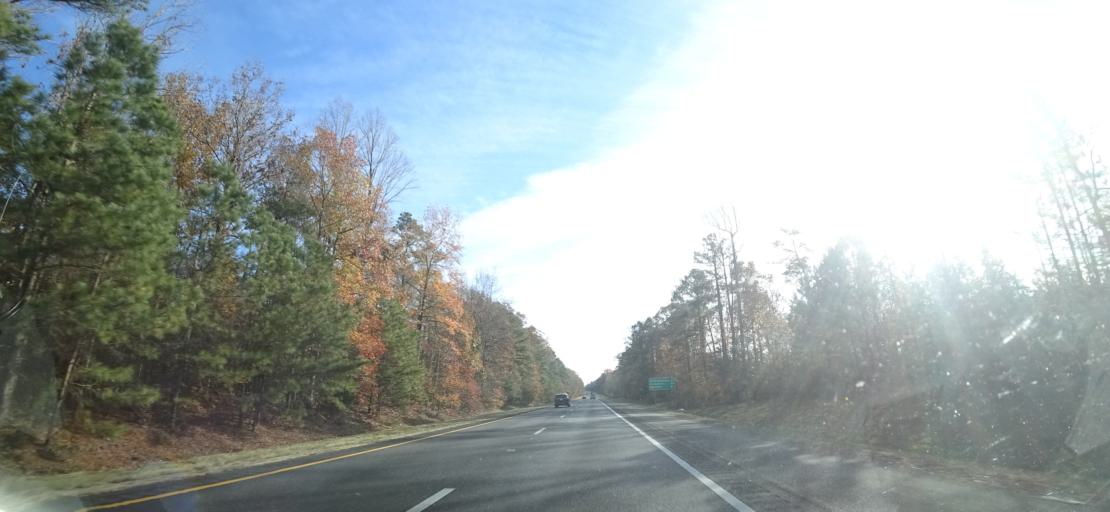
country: US
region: Virginia
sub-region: New Kent County
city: New Kent
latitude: 37.5012
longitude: -77.0688
